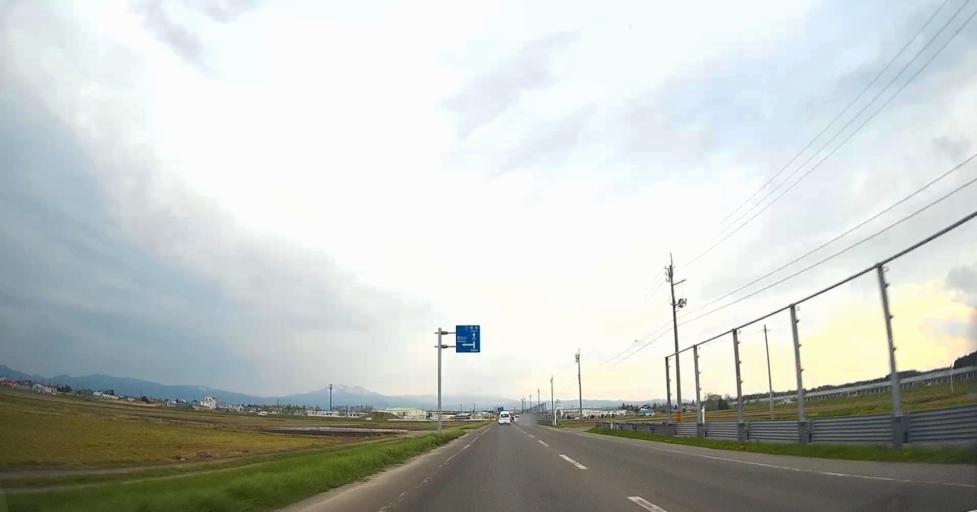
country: JP
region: Aomori
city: Aomori Shi
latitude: 40.8652
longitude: 140.6795
